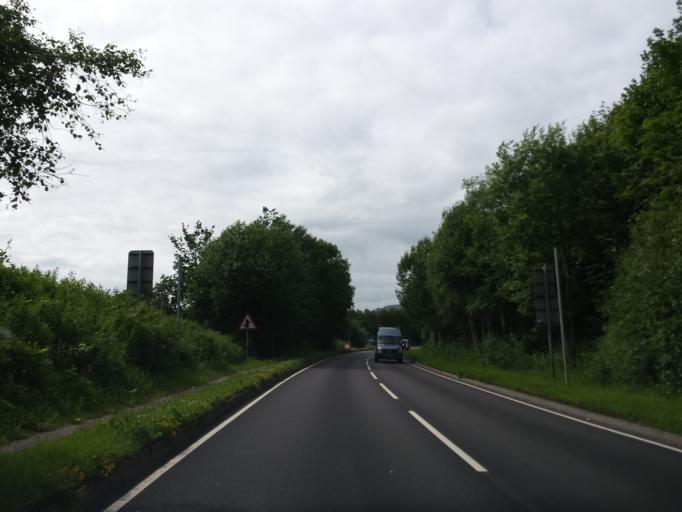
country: GB
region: Scotland
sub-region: Highland
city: Fort William
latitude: 56.8432
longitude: -5.1463
